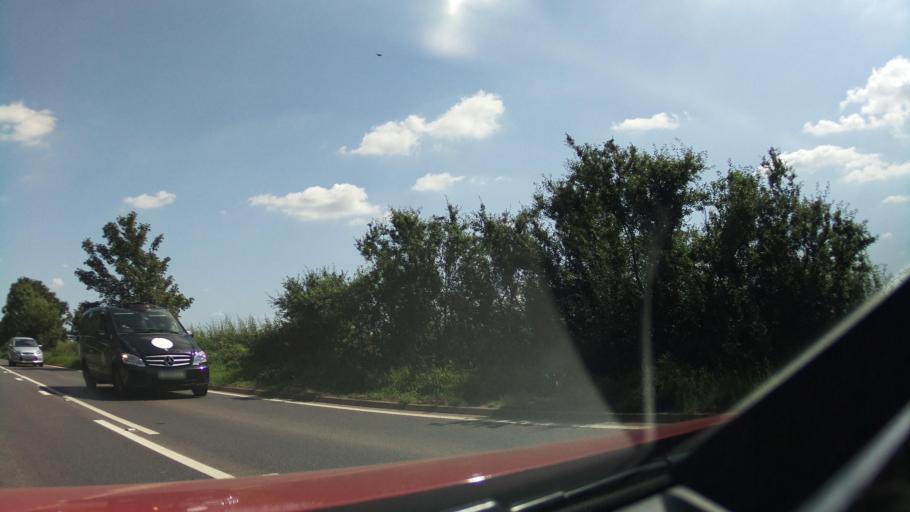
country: GB
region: England
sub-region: Warwickshire
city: Nuneaton
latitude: 52.5483
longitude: -1.4508
